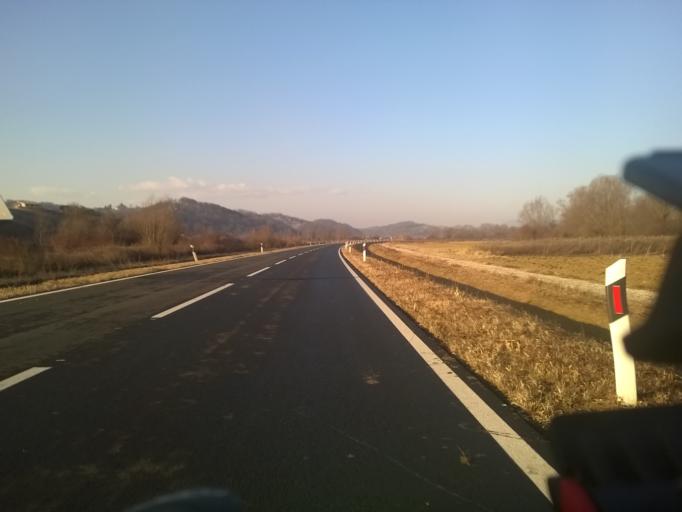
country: HR
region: Krapinsko-Zagorska
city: Zabok
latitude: 46.0393
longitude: 15.9174
